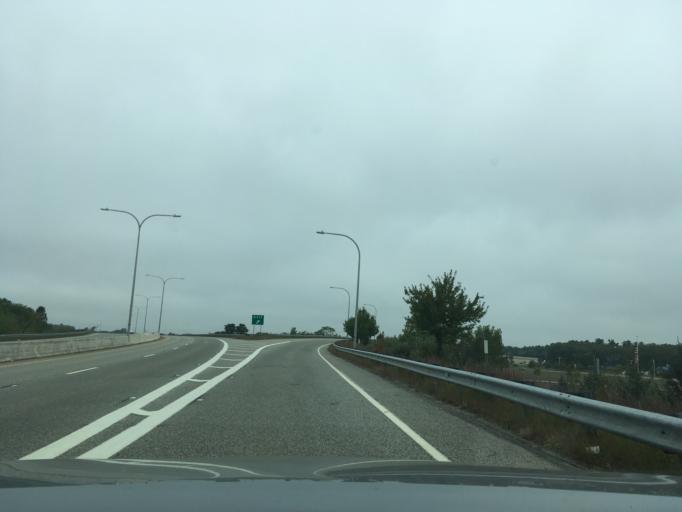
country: US
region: Rhode Island
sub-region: Washington County
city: North Kingstown
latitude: 41.6027
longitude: -71.4463
